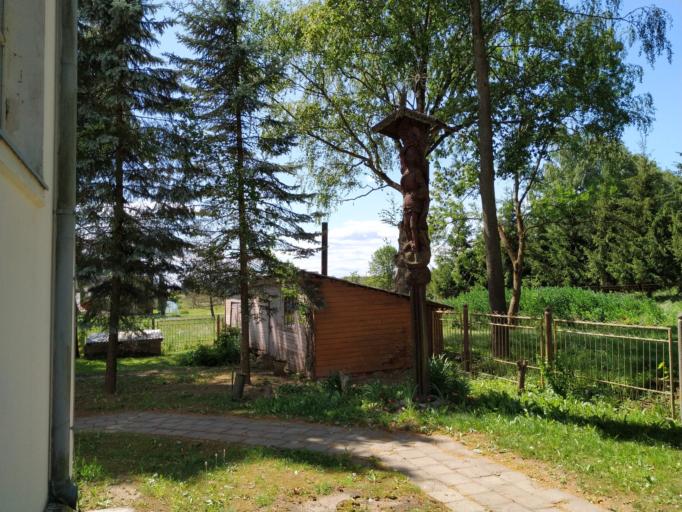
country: LT
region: Panevezys
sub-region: Birzai
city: Birzai
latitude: 56.2530
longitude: 24.5436
